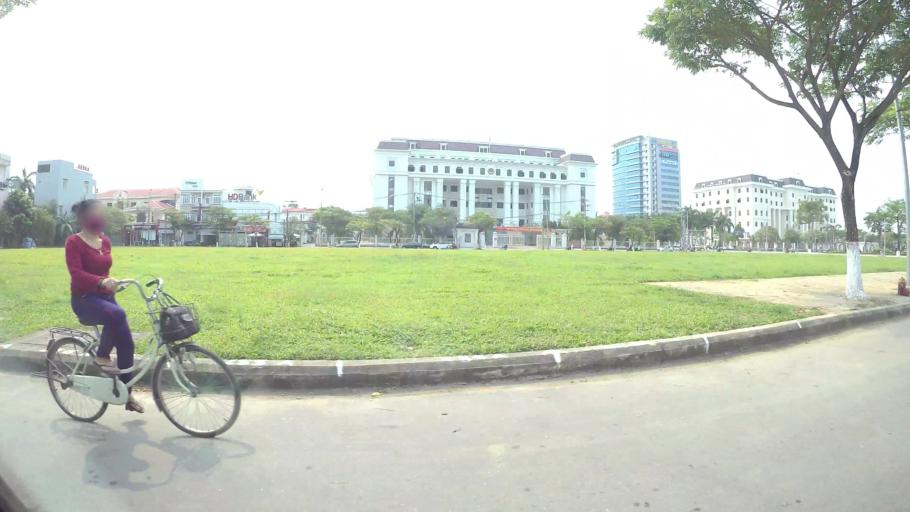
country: VN
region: Da Nang
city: Son Tra
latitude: 16.0398
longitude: 108.2224
